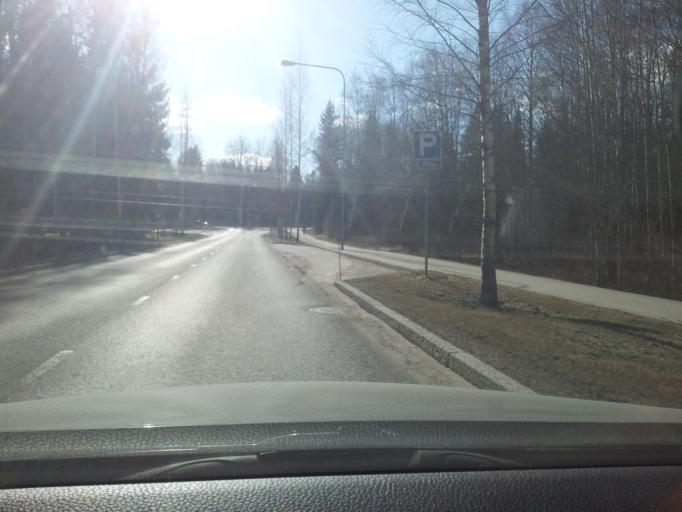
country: FI
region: Uusimaa
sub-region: Helsinki
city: Koukkuniemi
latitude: 60.1665
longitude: 24.7904
